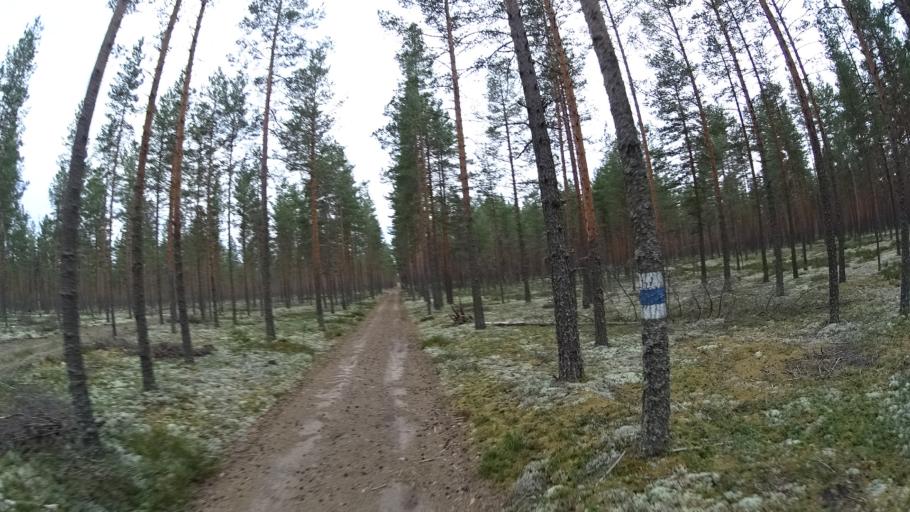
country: FI
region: Satakunta
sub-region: Pohjois-Satakunta
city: Jaemijaervi
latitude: 61.7660
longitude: 22.8010
